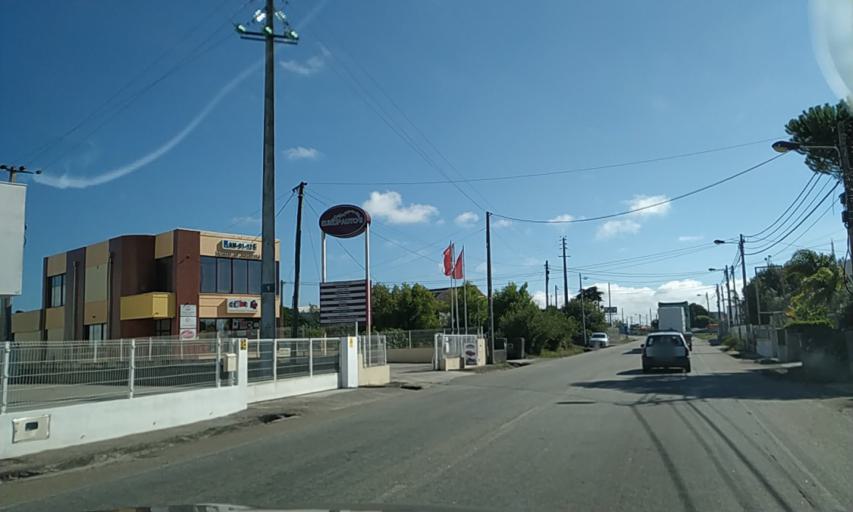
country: PT
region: Aveiro
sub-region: Aveiro
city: Aveiro
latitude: 40.6727
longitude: -8.6044
